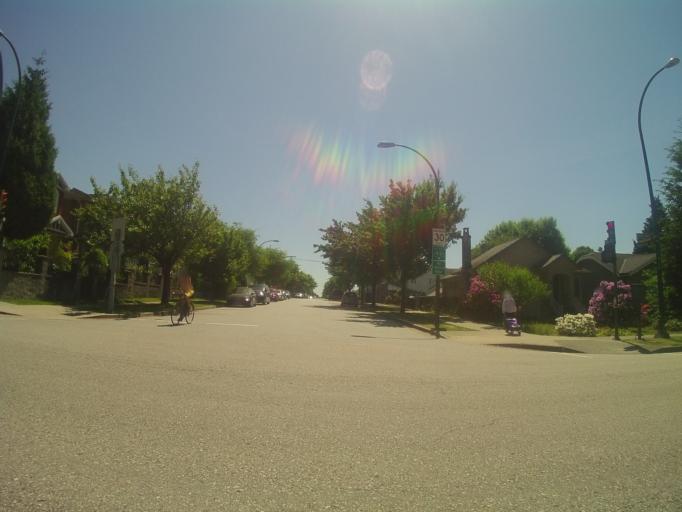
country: CA
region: British Columbia
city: Vancouver
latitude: 49.2489
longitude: -123.1050
